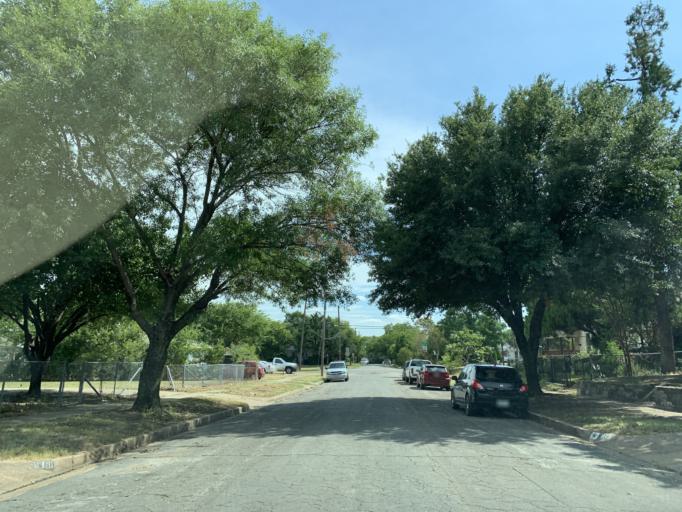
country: US
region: Texas
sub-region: Dallas County
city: Cockrell Hill
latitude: 32.7380
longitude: -96.8430
